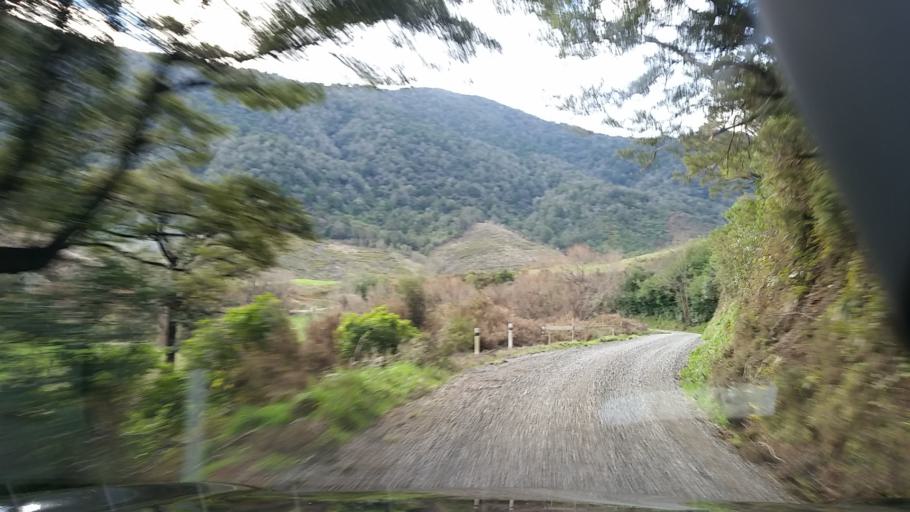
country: NZ
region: Nelson
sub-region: Nelson City
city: Nelson
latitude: -41.1911
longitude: 173.6372
